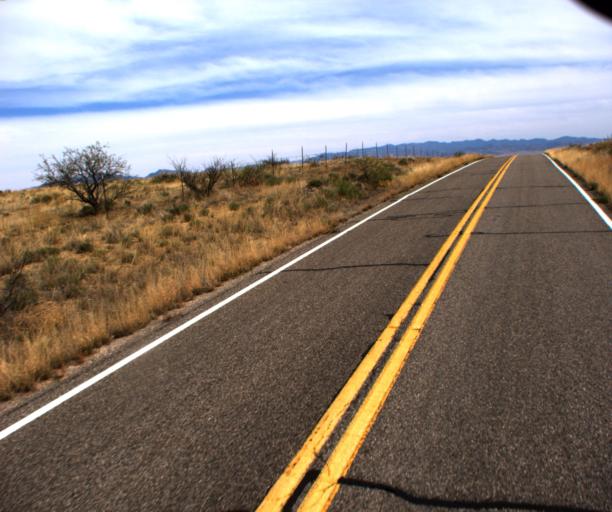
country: US
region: Arizona
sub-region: Cochise County
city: Willcox
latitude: 32.1361
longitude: -109.5617
